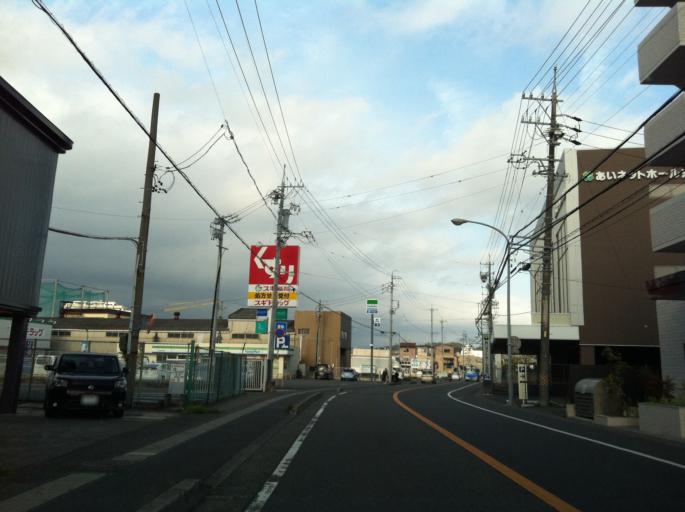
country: JP
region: Shizuoka
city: Shizuoka-shi
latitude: 34.9828
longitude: 138.4184
